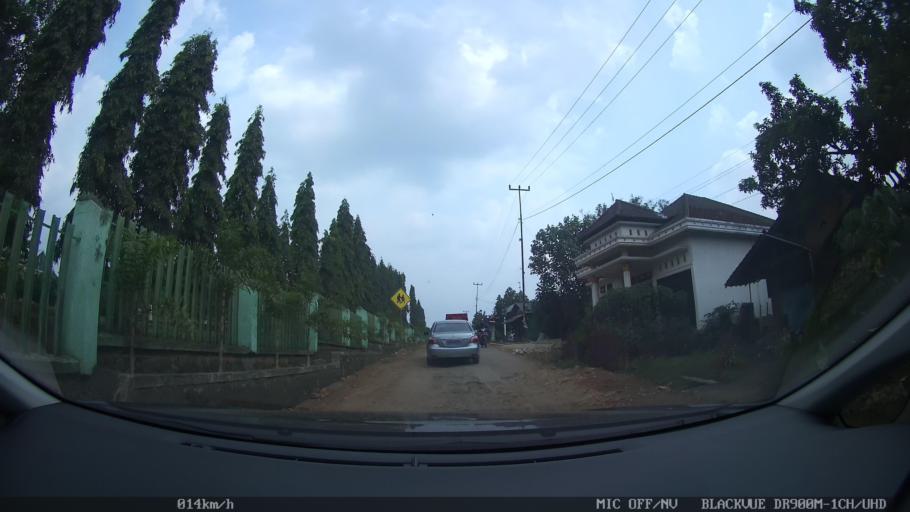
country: ID
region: Lampung
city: Gadingrejo
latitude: -5.3619
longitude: 105.0252
